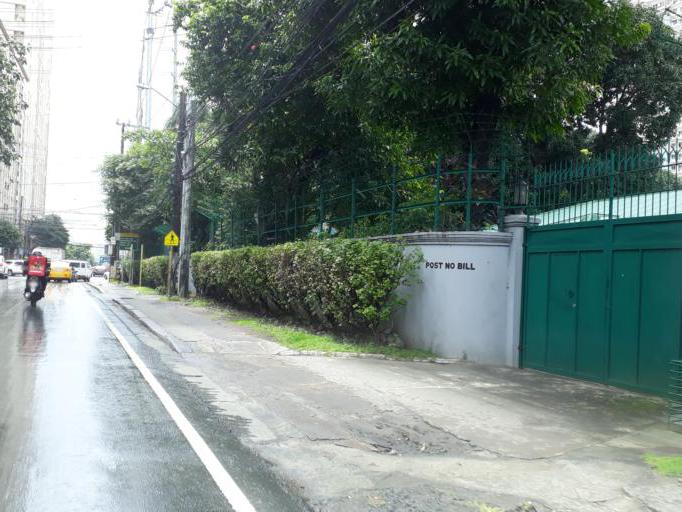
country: PH
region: Metro Manila
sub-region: San Juan
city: San Juan
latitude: 14.6126
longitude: 121.0355
